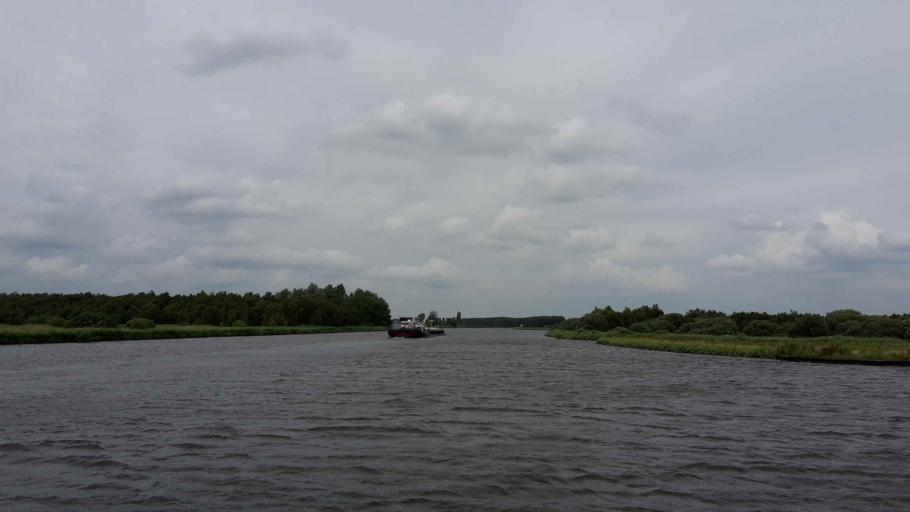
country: NL
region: Friesland
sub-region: Gemeente Boarnsterhim
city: Warten
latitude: 53.1271
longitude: 5.8819
